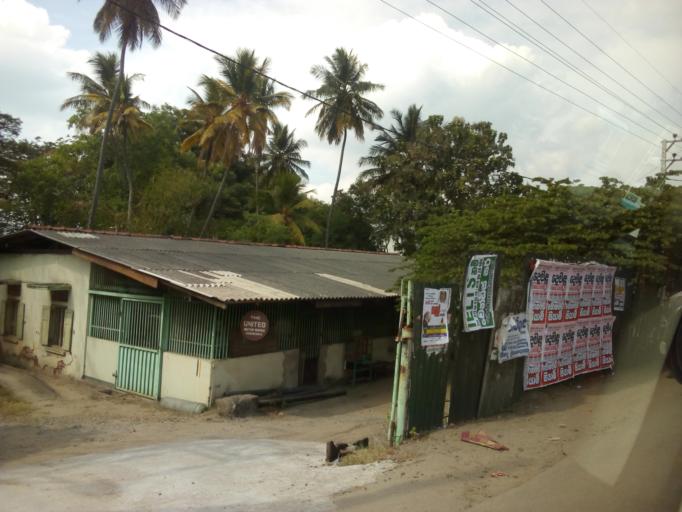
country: LK
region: North Western
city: Kurunegala
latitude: 7.4904
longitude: 80.3651
